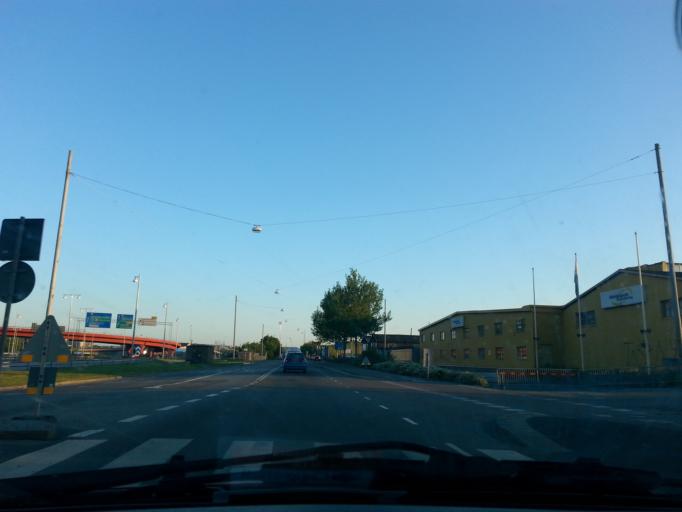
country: SE
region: Vaestra Goetaland
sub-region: Goteborg
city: Goeteborg
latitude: 57.7285
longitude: 11.9974
